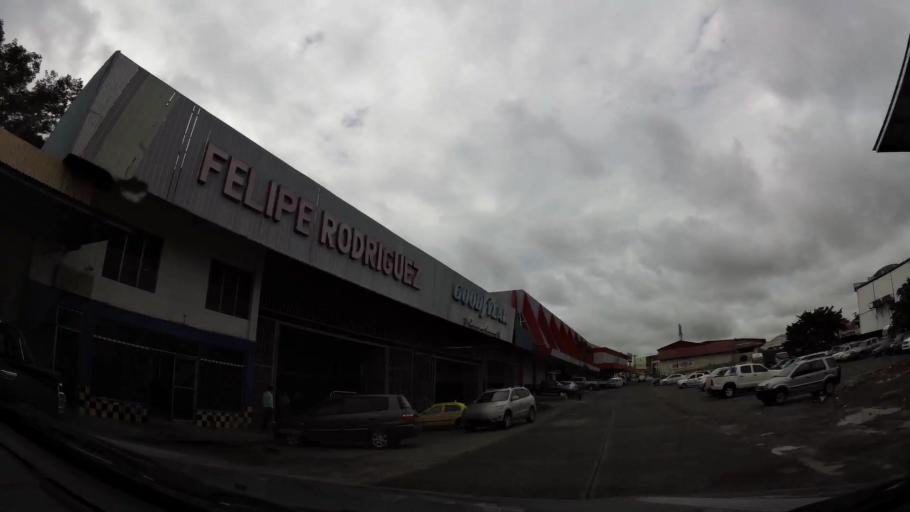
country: PA
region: Chiriqui
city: David
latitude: 8.4359
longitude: -82.4229
